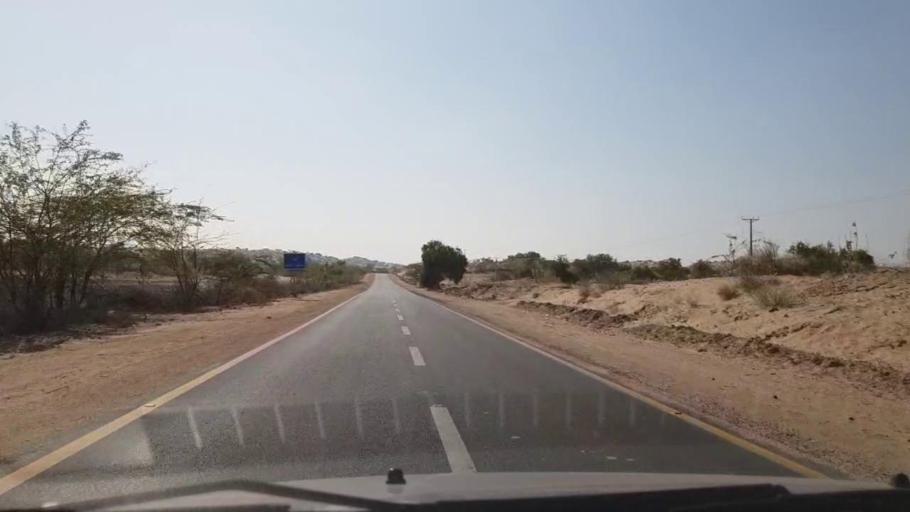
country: PK
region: Sindh
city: Diplo
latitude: 24.5001
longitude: 69.6062
